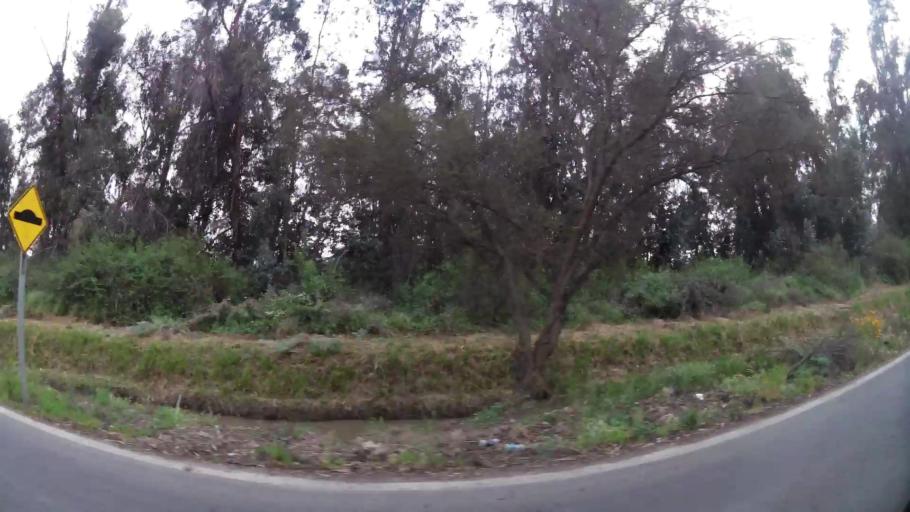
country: CL
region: Santiago Metropolitan
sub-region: Provincia de Chacabuco
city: Chicureo Abajo
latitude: -33.2728
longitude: -70.7037
